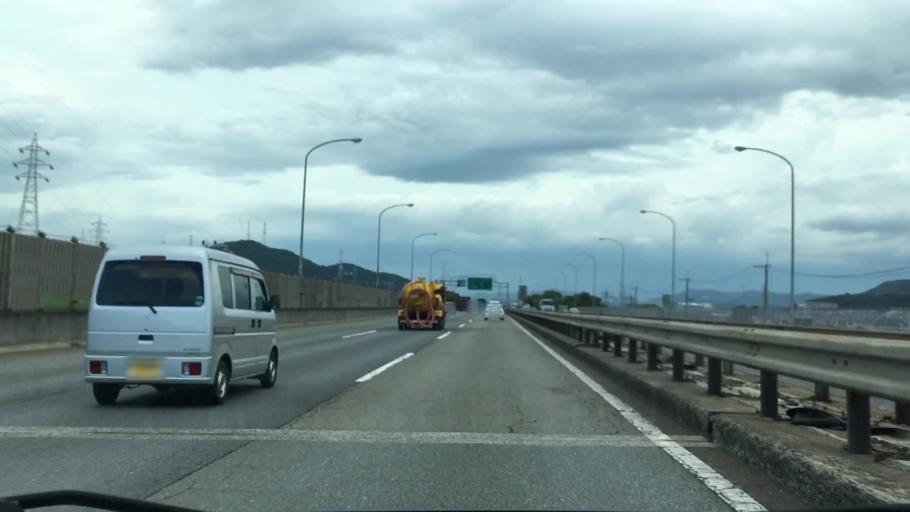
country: JP
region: Hyogo
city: Shirahamacho-usazakiminami
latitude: 34.7944
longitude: 134.7640
